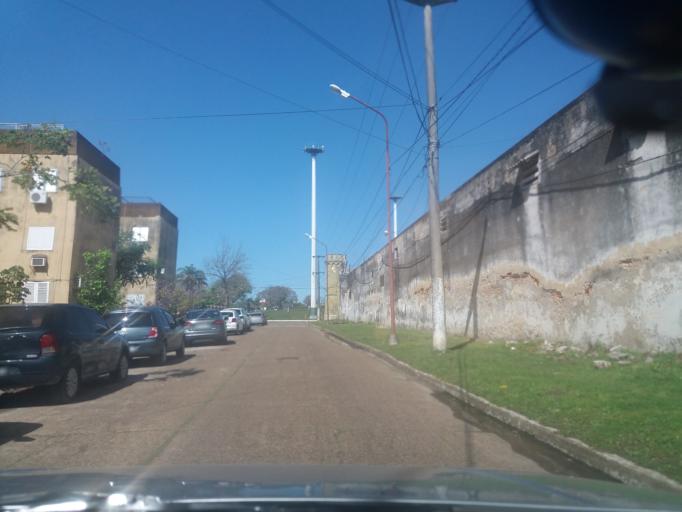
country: AR
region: Corrientes
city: Corrientes
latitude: -27.4730
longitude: -58.8499
